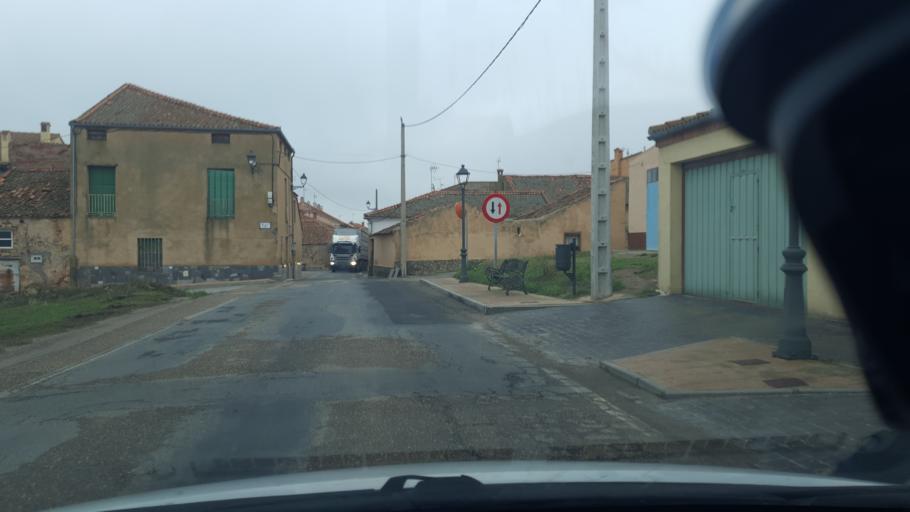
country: ES
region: Castille and Leon
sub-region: Provincia de Segovia
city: Valseca
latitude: 40.9987
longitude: -4.1758
